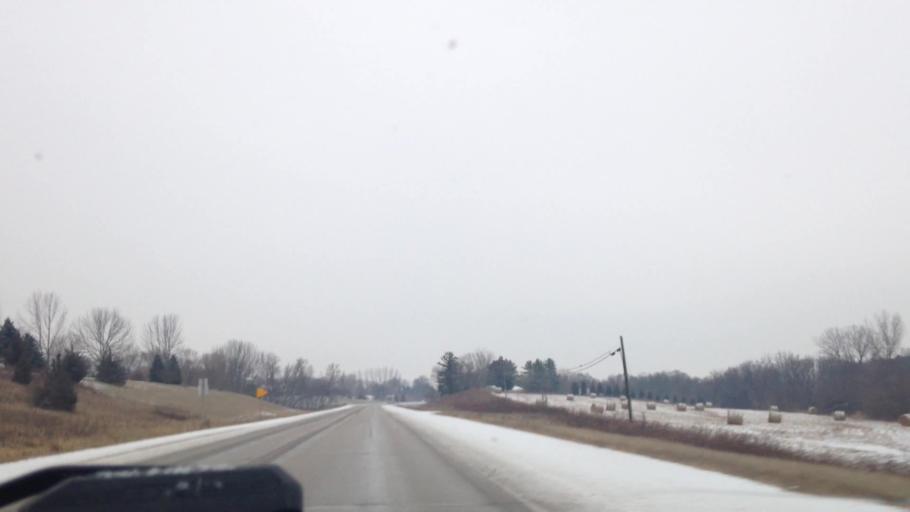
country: US
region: Wisconsin
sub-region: Dodge County
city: Mayville
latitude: 43.4403
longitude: -88.5432
